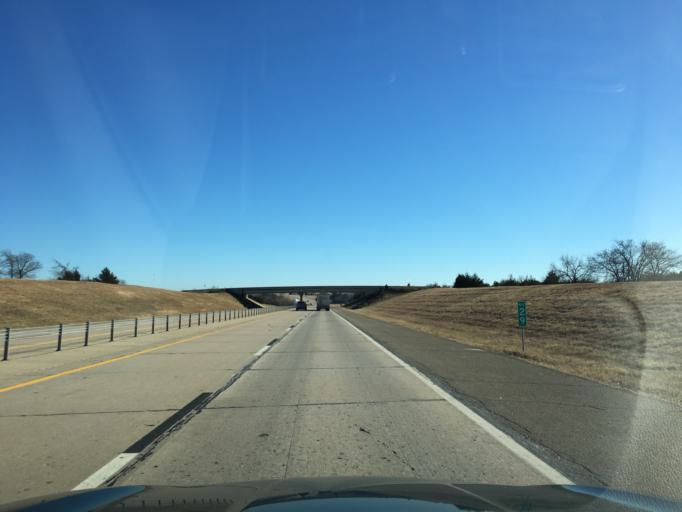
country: US
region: Oklahoma
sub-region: Pawnee County
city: Pawnee
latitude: 36.2344
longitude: -96.9185
